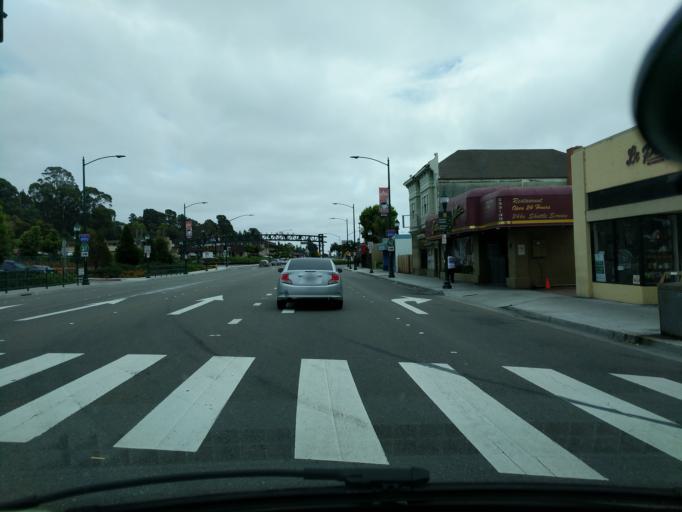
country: US
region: California
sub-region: Alameda County
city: Hayward
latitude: 37.6698
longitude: -122.0819
